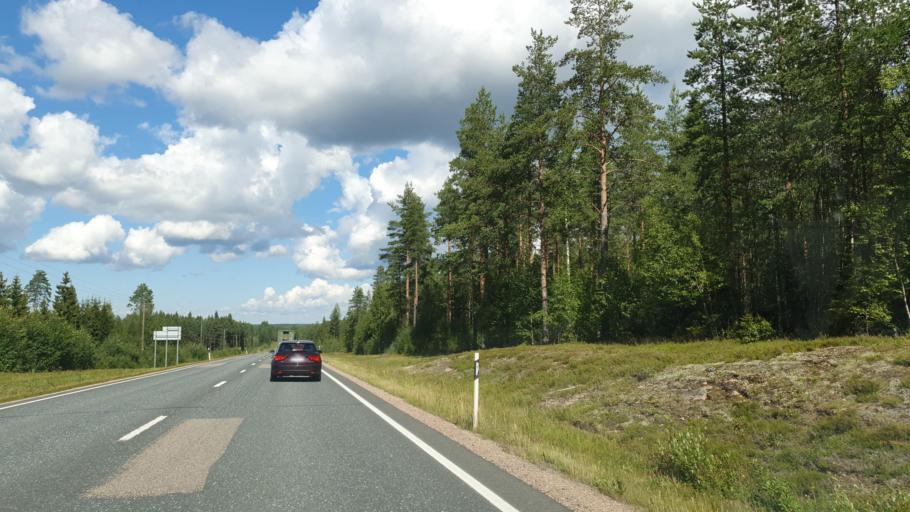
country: FI
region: Kainuu
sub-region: Kajaani
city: Kajaani
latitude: 64.0982
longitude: 27.4499
